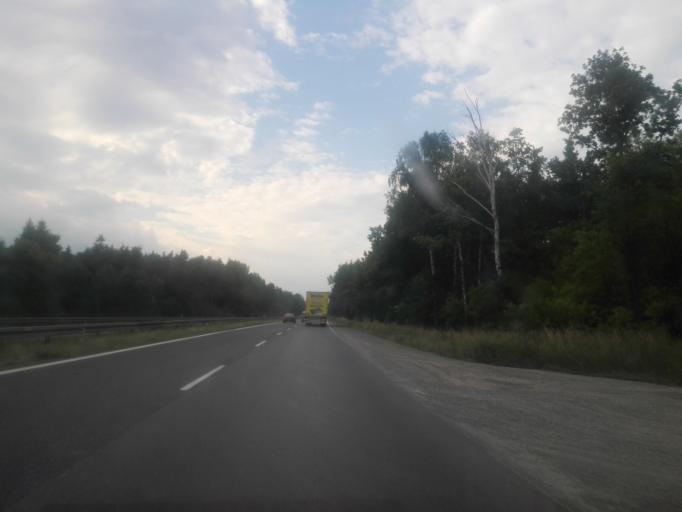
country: PL
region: Silesian Voivodeship
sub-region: Powiat bedzinski
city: Siewierz
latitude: 50.5165
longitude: 19.1943
